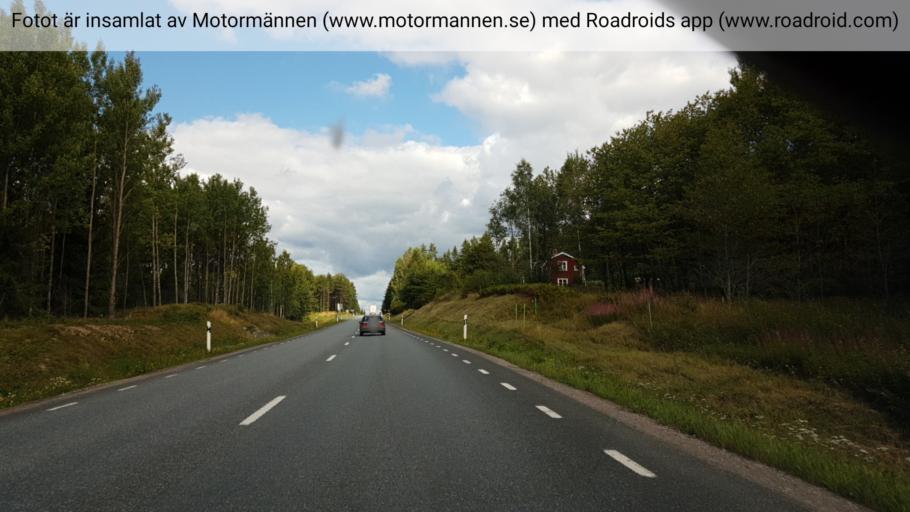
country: SE
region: Joenkoeping
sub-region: Aneby Kommun
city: Aneby
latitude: 57.8650
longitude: 14.8671
